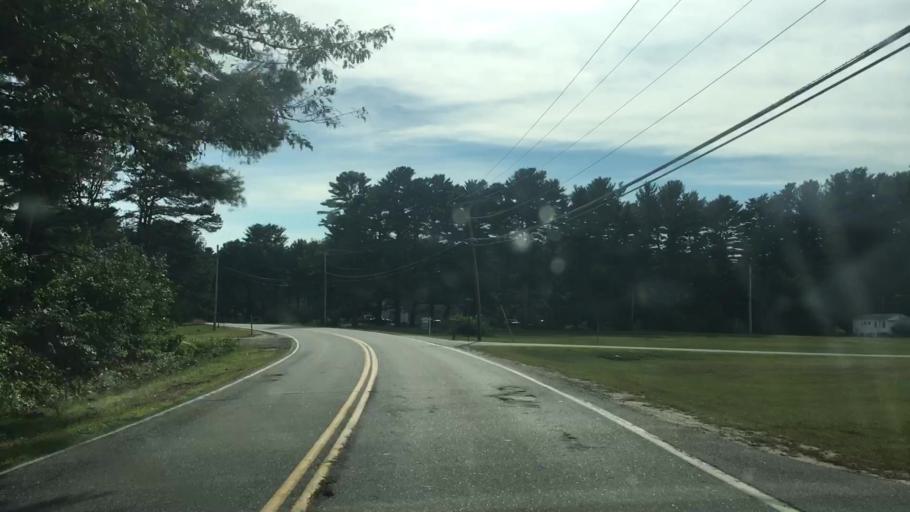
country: US
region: Maine
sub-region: Sagadahoc County
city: Bath
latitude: 43.9308
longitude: -69.8885
